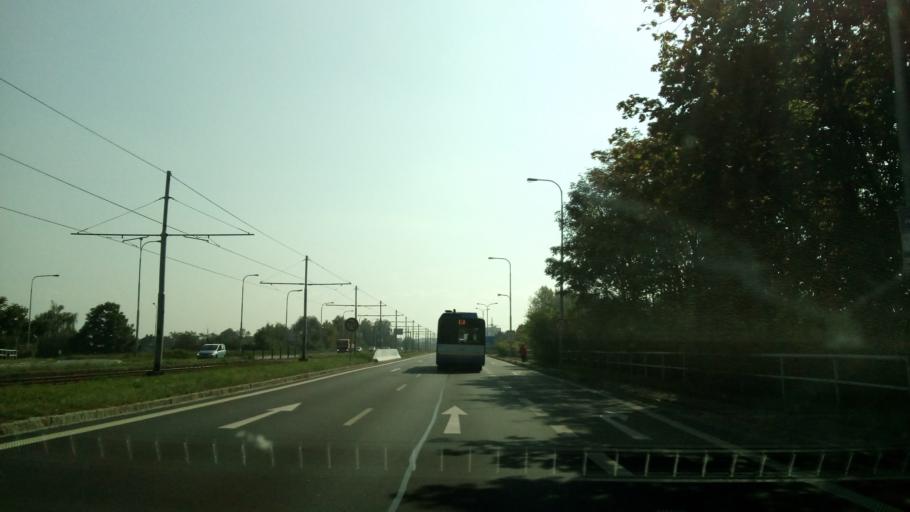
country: CZ
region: Moravskoslezsky
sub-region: Okres Ostrava-Mesto
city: Ostrava
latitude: 49.8011
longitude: 18.2464
